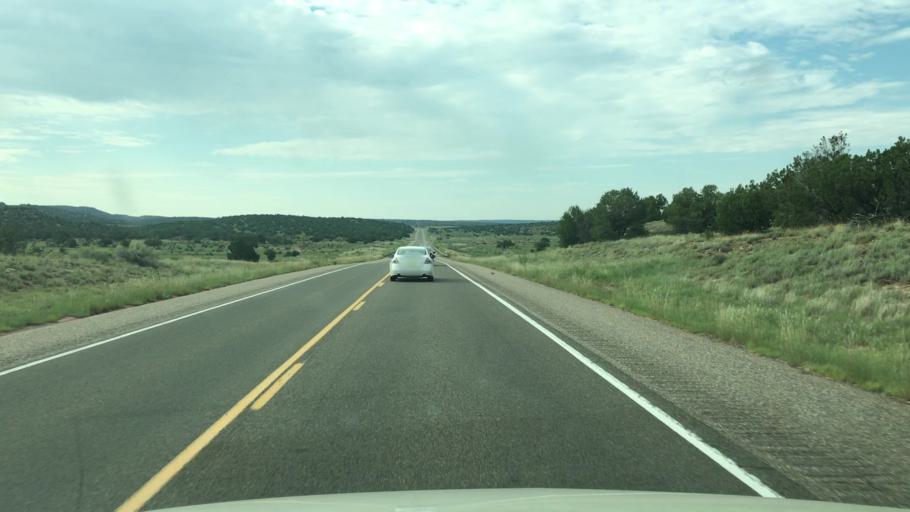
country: US
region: New Mexico
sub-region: Santa Fe County
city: Eldorado at Santa Fe
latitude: 35.3110
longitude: -105.8297
